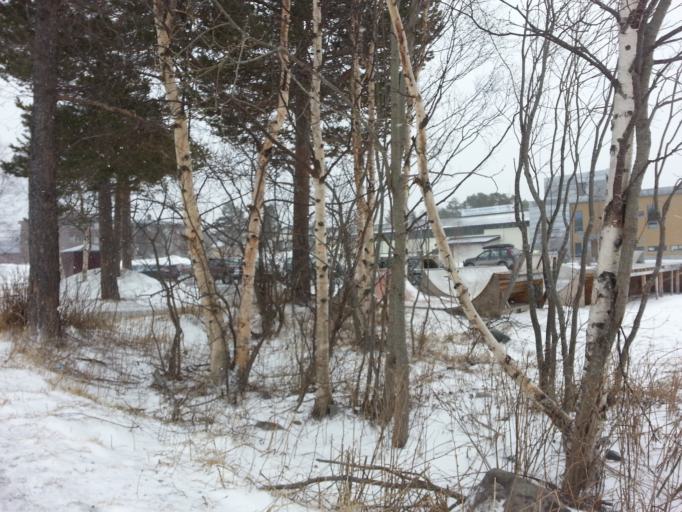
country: NO
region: Sor-Trondelag
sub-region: Oppdal
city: Oppdal
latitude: 62.5955
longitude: 9.6837
